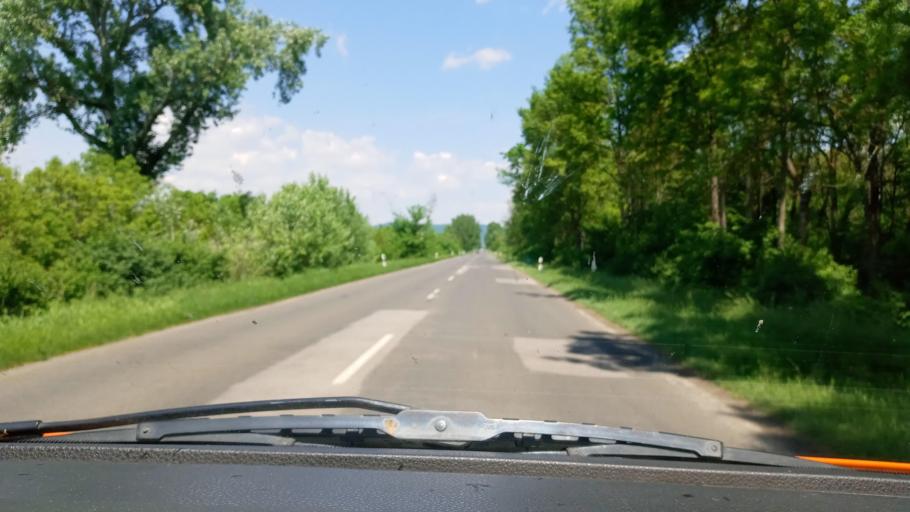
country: HU
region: Baranya
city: Harkany
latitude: 45.8212
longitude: 18.2175
